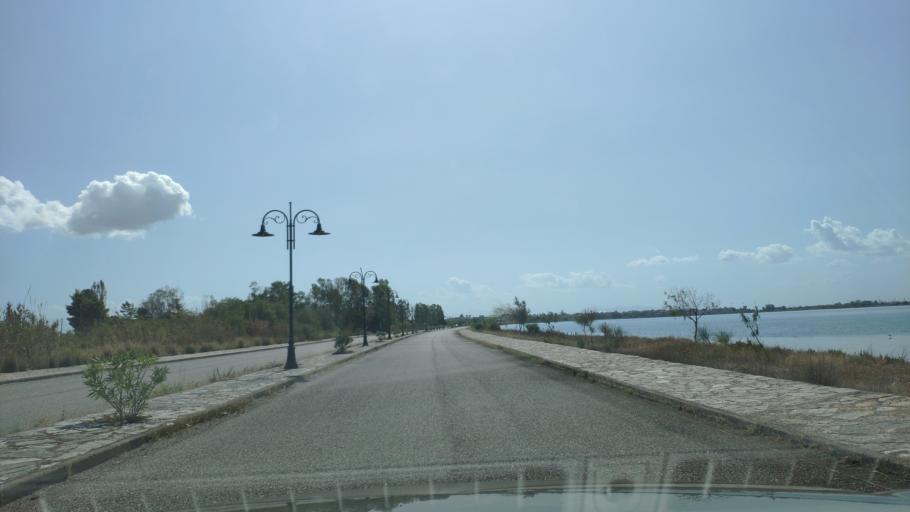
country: GR
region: West Greece
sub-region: Nomos Aitolias kai Akarnanias
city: Mesolongi
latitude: 38.3847
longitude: 21.4192
